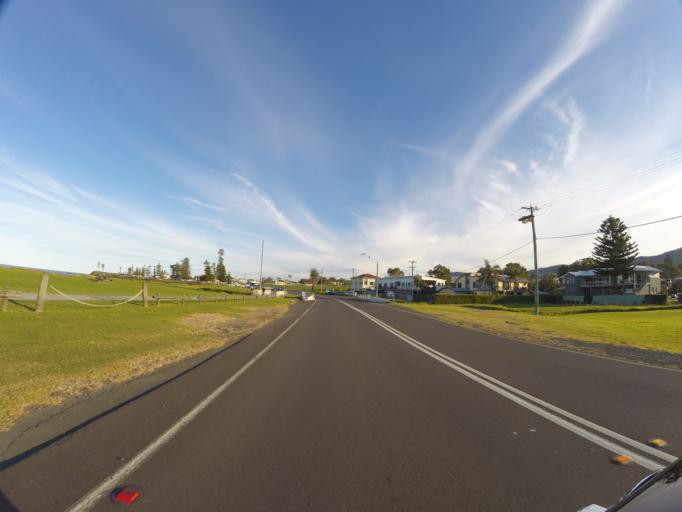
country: AU
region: New South Wales
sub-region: Wollongong
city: Bulli
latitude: -34.3338
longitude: 150.9243
